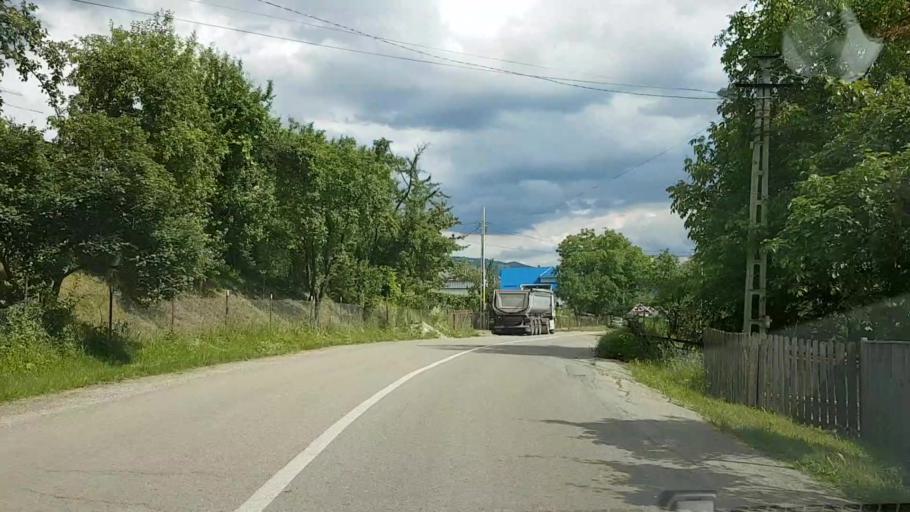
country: RO
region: Neamt
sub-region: Comuna Hangu
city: Hangu
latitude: 47.0254
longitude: 26.0686
